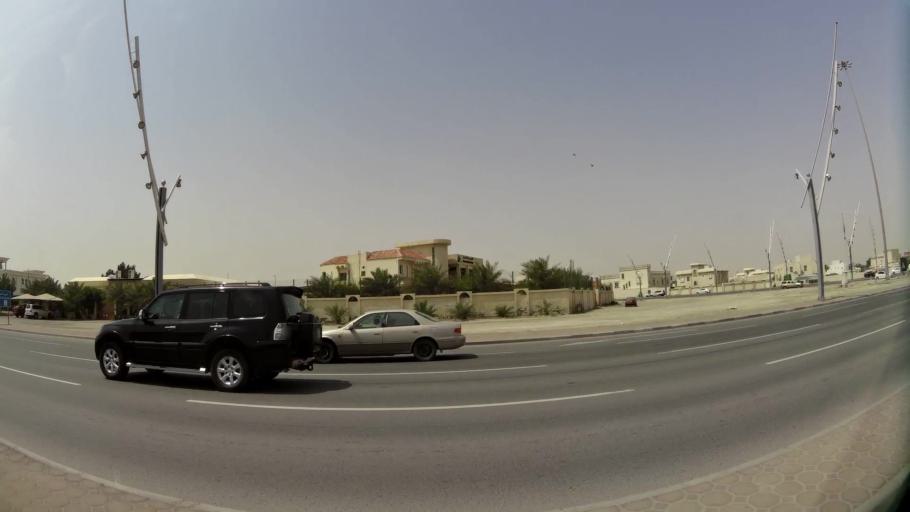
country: QA
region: Baladiyat ar Rayyan
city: Ar Rayyan
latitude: 25.2511
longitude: 51.4312
